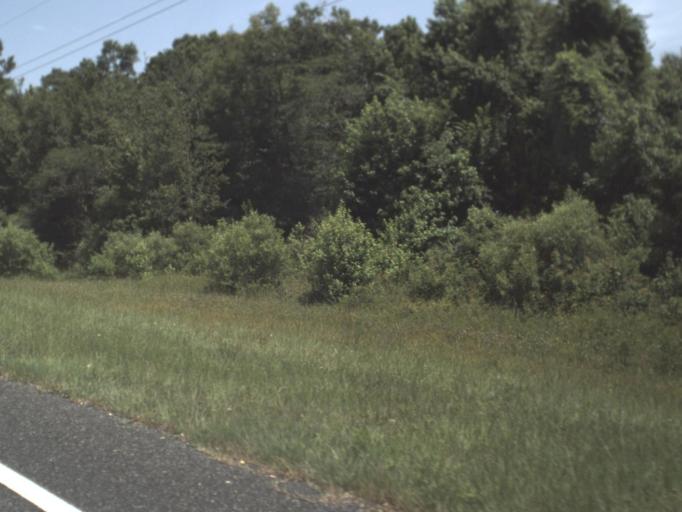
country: US
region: Florida
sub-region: Taylor County
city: Steinhatchee
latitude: 29.6865
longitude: -83.2674
